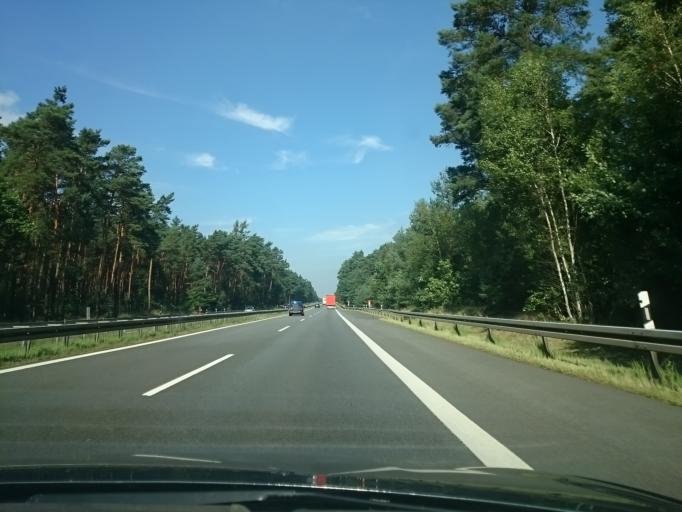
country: DE
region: Brandenburg
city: Bronkow
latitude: 51.7222
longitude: 13.8830
